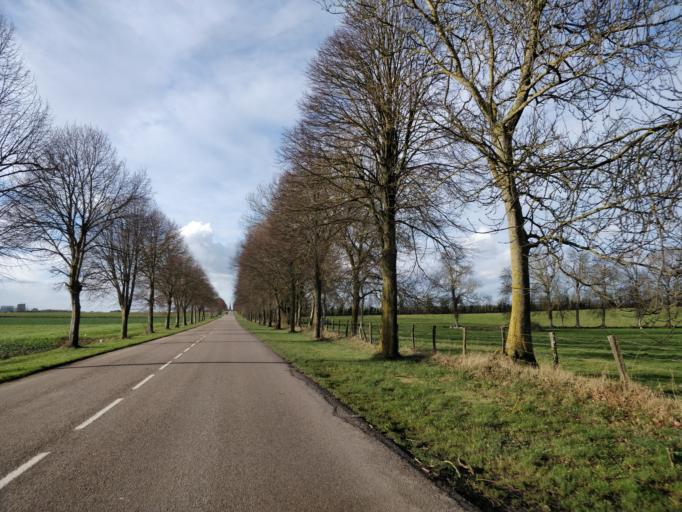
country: FR
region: Lower Normandy
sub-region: Departement du Calvados
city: Rots
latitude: 49.2029
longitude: -0.4866
